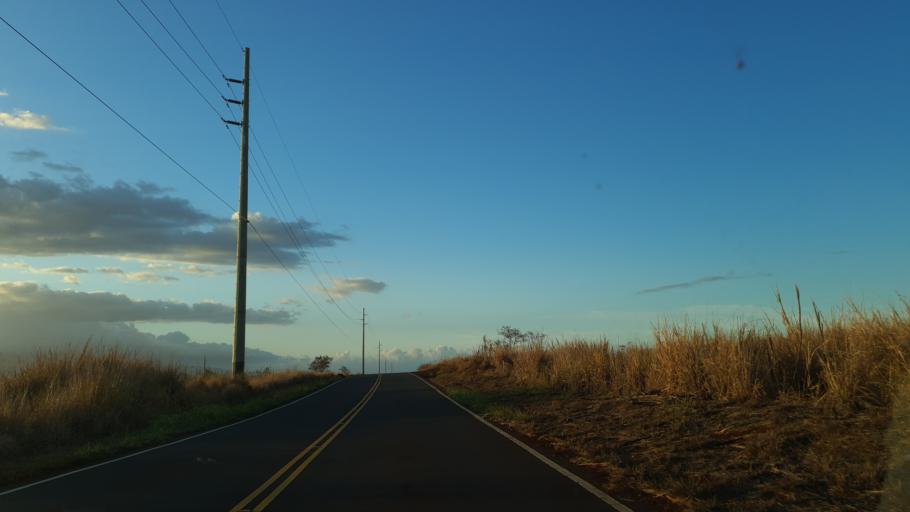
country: US
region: Hawaii
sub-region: Maui County
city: Pukalani
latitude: 20.8070
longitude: -156.3798
